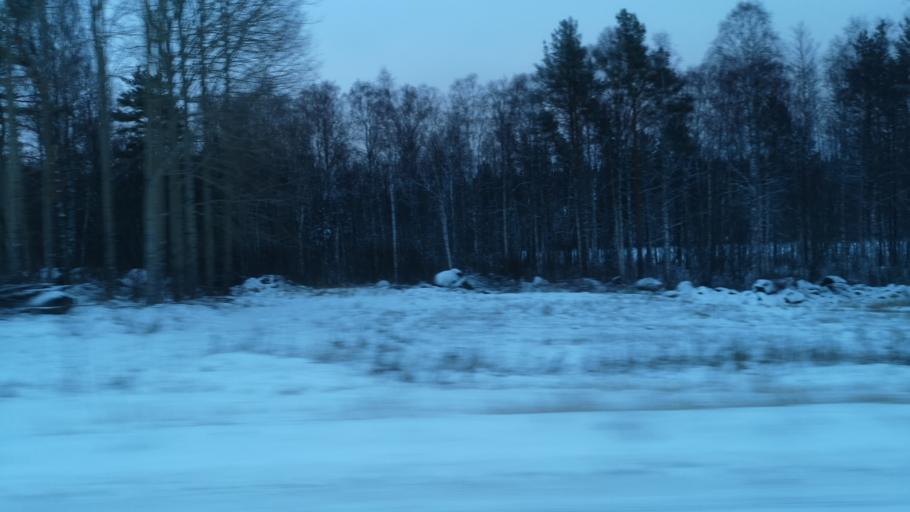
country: FI
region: Southern Savonia
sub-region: Savonlinna
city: Enonkoski
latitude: 62.1027
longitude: 28.6479
